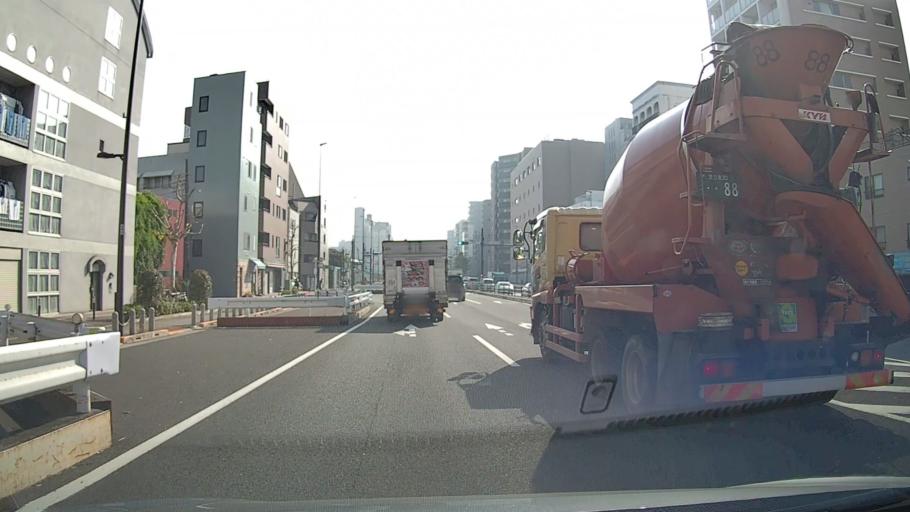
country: JP
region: Tokyo
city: Tokyo
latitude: 35.7392
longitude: 139.7328
